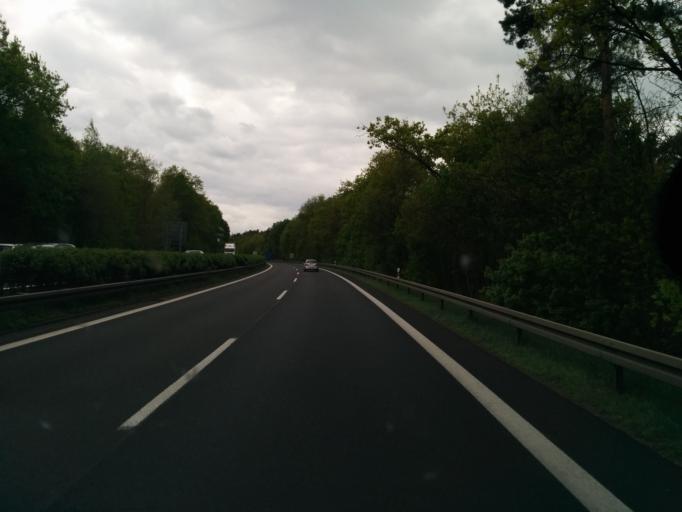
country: DE
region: Brandenburg
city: Gross Kreutz
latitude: 52.3934
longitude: 12.8335
